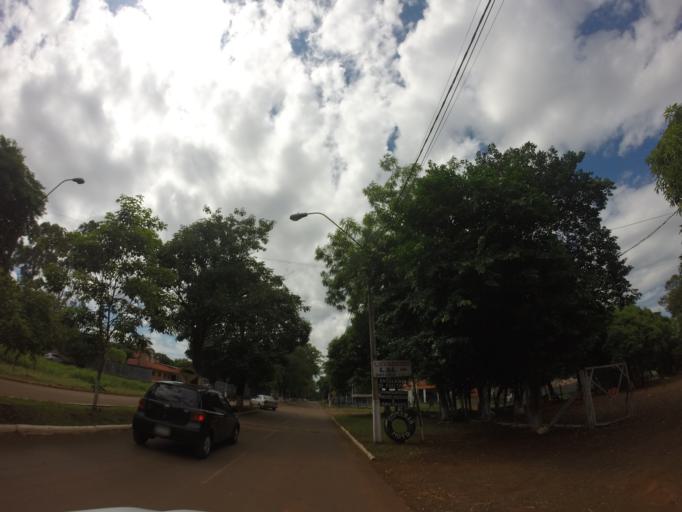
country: PY
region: Alto Parana
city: Ciudad del Este
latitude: -25.4116
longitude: -54.6384
